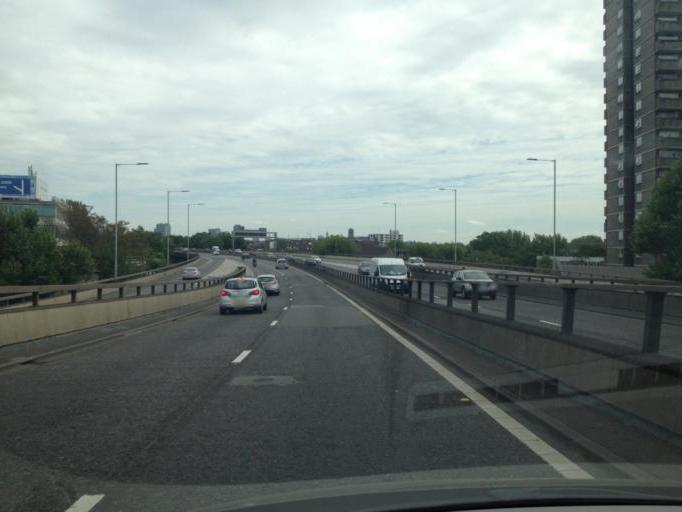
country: GB
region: England
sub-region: Greater London
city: Hammersmith
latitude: 51.5156
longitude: -0.2184
